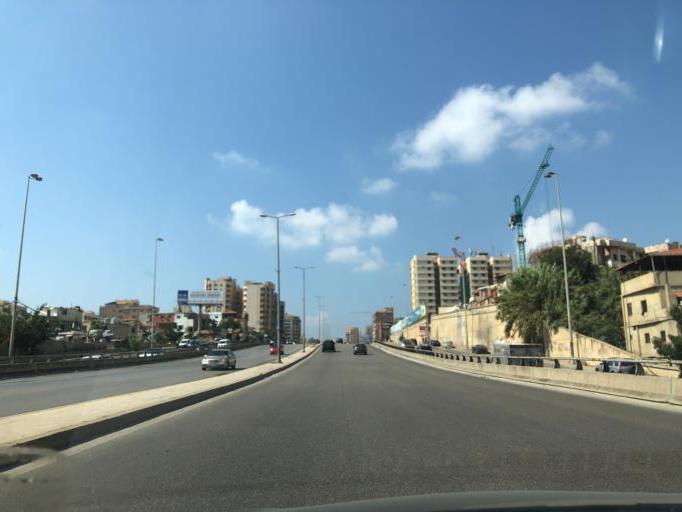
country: LB
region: Beyrouth
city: Beirut
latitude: 33.8616
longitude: 35.4859
